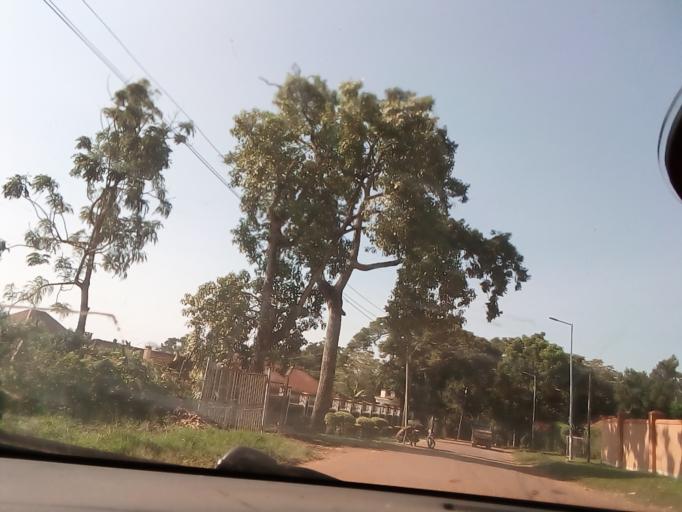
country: UG
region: Central Region
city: Masaka
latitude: -0.3372
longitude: 31.7353
